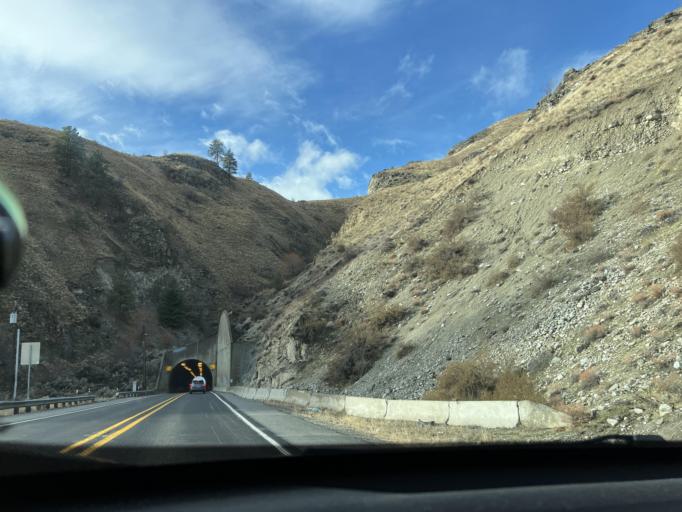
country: US
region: Washington
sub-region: Chelan County
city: Manson
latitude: 47.7795
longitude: -120.1434
